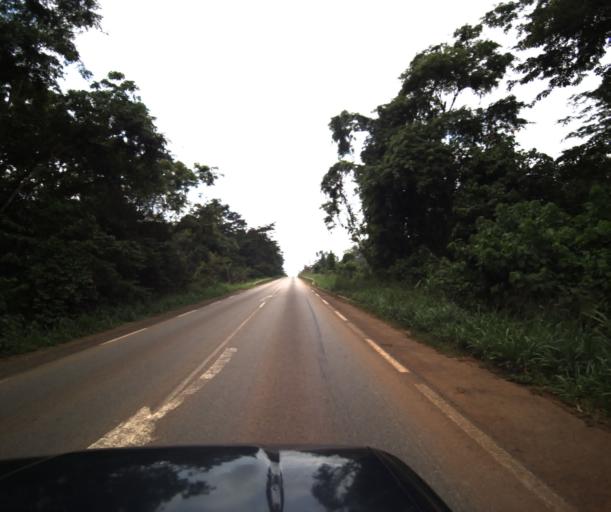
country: CM
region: Centre
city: Eseka
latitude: 3.8636
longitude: 10.9232
